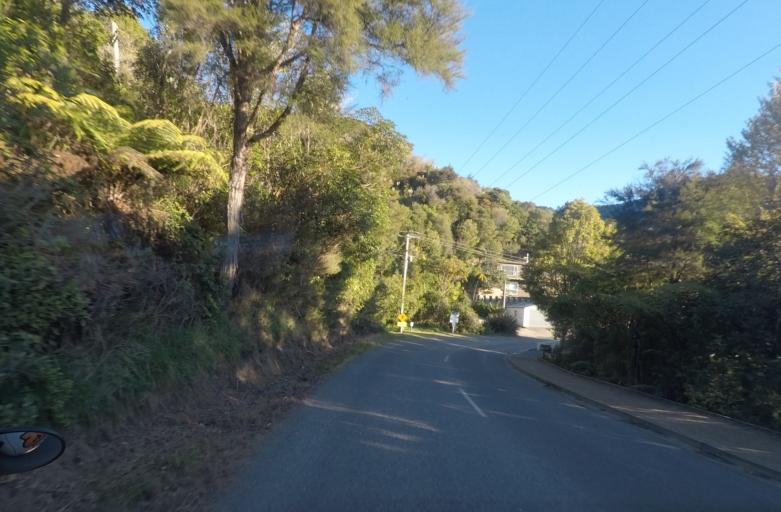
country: NZ
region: Marlborough
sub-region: Marlborough District
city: Picton
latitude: -41.2749
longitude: 173.9663
